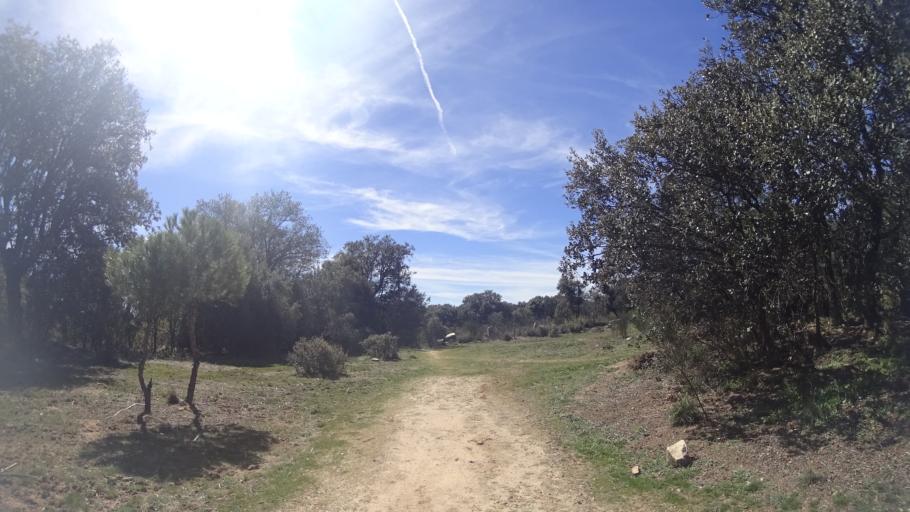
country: ES
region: Madrid
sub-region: Provincia de Madrid
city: Galapagar
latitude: 40.5894
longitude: -3.9844
